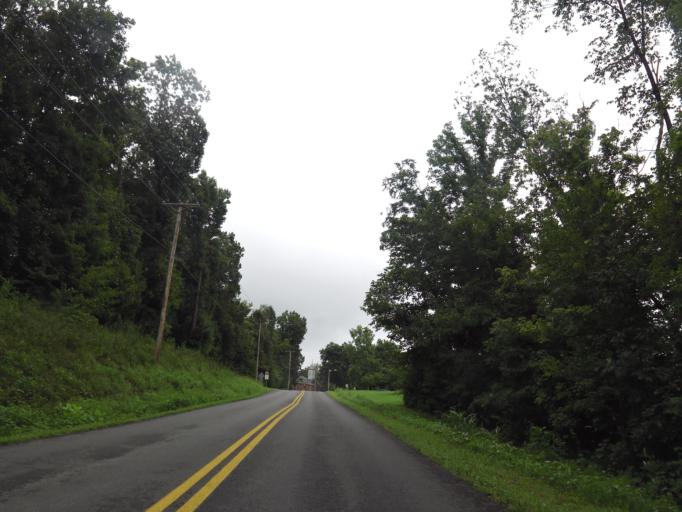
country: US
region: Missouri
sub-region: Cape Girardeau County
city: Cape Girardeau
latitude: 37.3542
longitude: -89.5619
